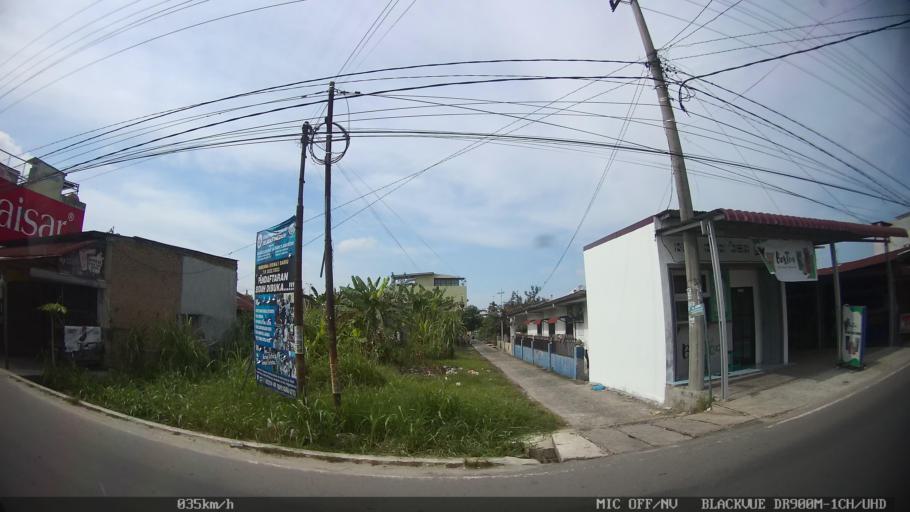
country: ID
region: North Sumatra
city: Percut
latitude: 3.6078
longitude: 98.7801
